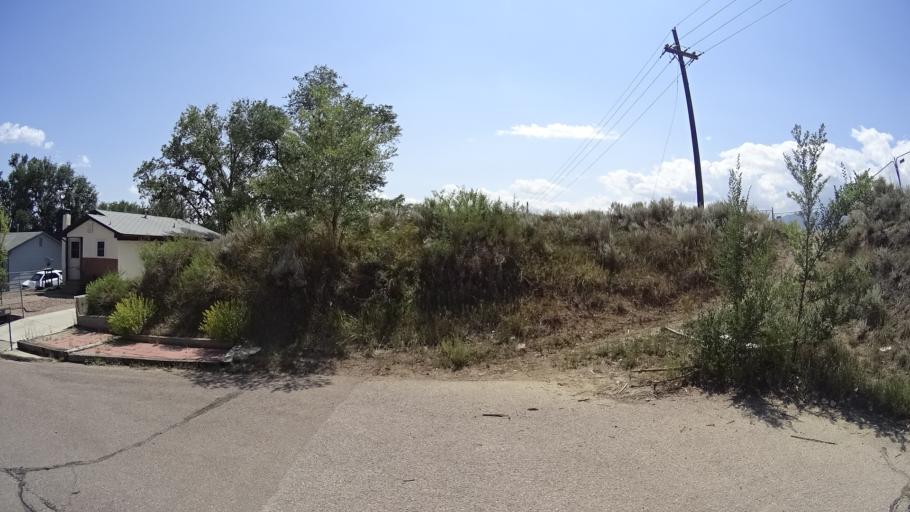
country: US
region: Colorado
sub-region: El Paso County
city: Colorado Springs
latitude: 38.8655
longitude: -104.8403
